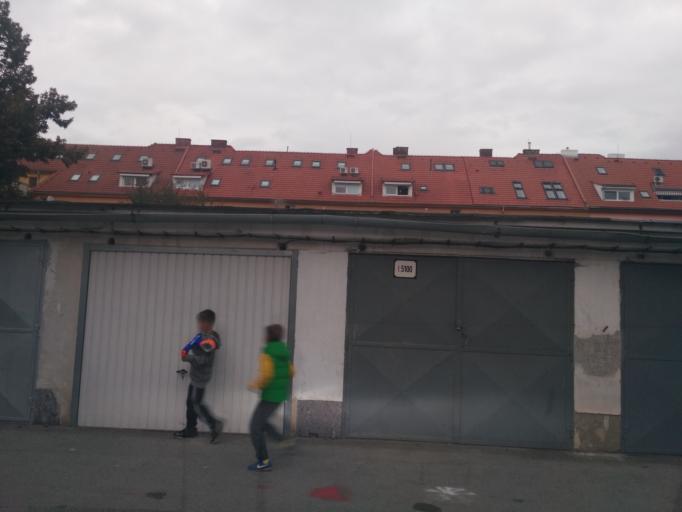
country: SK
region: Kosicky
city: Kosice
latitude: 48.7290
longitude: 21.2447
